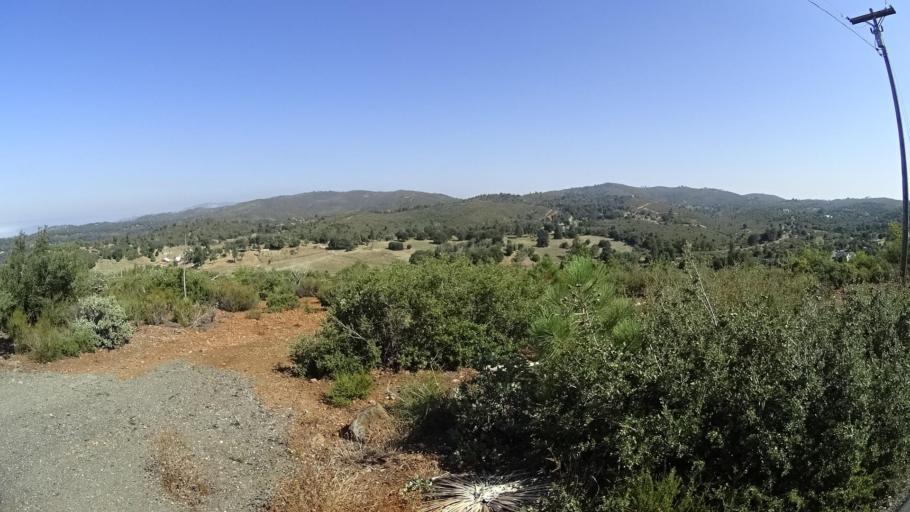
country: US
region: California
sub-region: San Diego County
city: Julian
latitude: 33.0254
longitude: -116.5791
